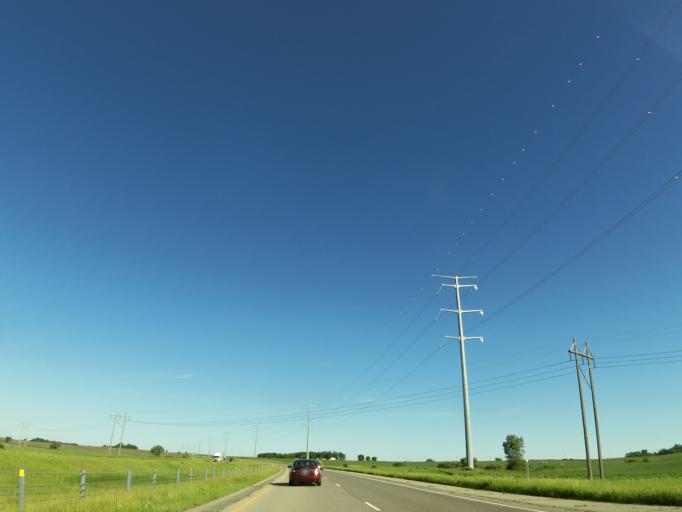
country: US
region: Minnesota
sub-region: Douglas County
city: Alexandria
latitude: 45.9611
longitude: -95.6228
